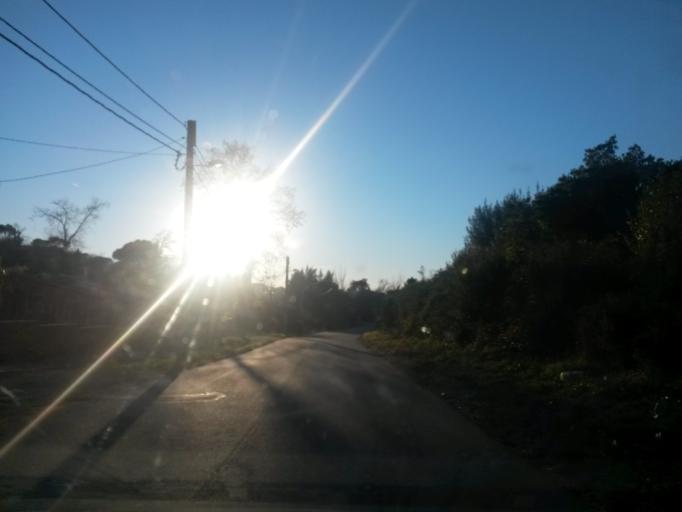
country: ES
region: Catalonia
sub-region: Provincia de Girona
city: Macanet de la Selva
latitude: 41.7506
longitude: 2.7054
